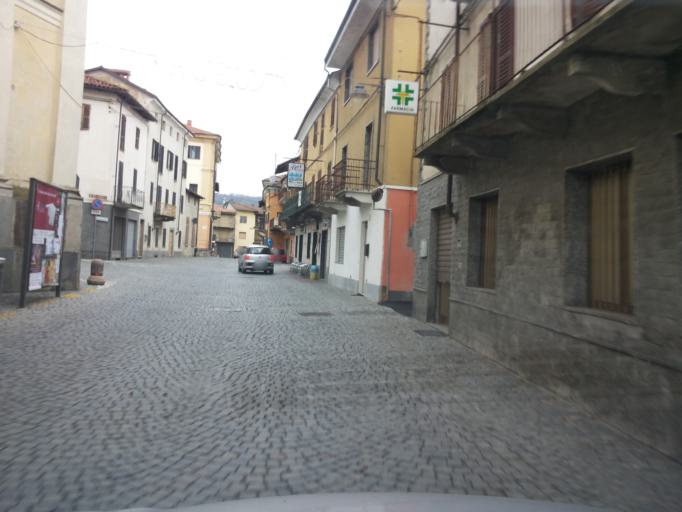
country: IT
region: Piedmont
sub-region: Provincia di Torino
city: Borgomasino
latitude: 45.3608
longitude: 7.9888
